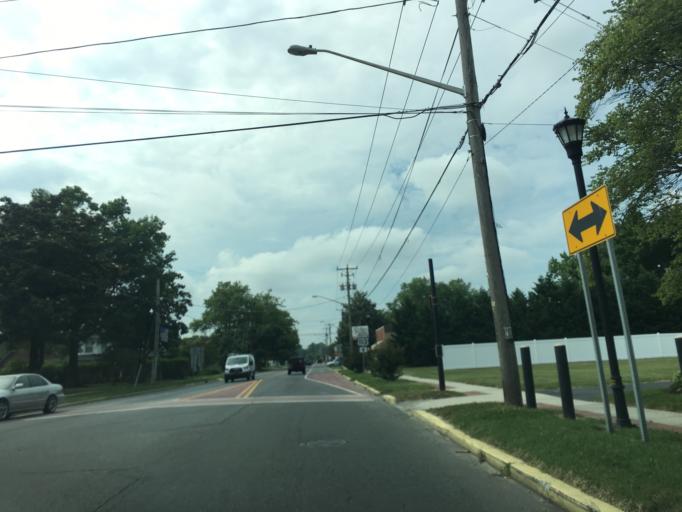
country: US
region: Delaware
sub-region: Sussex County
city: Millsboro
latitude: 38.5491
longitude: -75.2454
